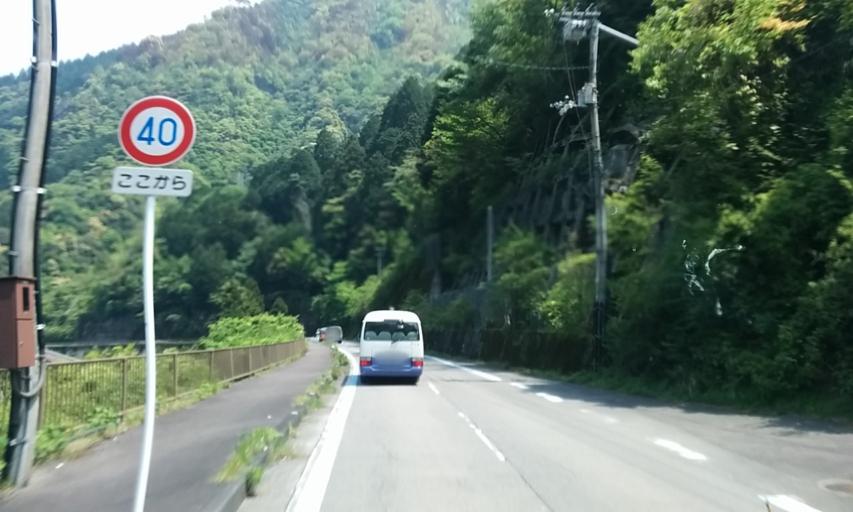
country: JP
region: Ehime
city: Niihama
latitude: 33.8895
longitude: 133.3081
